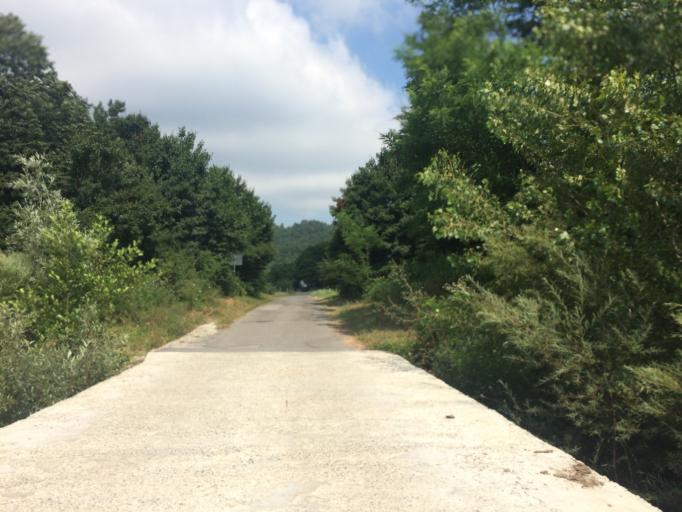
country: IT
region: Liguria
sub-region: Provincia di Savona
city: Dego
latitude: 44.4639
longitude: 8.3500
